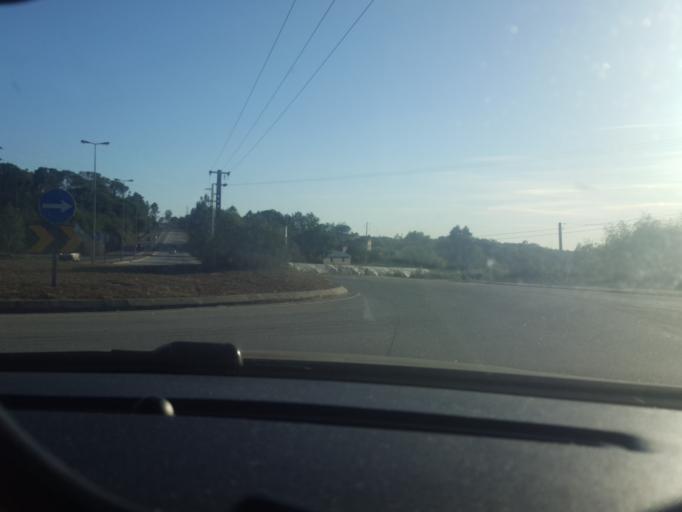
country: PT
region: Viseu
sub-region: Nelas
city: Nelas
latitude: 40.5339
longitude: -7.8625
